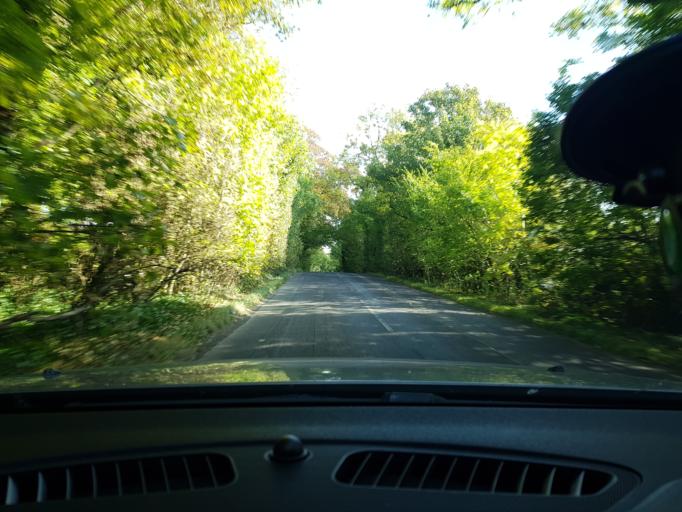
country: GB
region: England
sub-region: Borough of Swindon
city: Bishopstone
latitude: 51.5265
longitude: -1.6636
